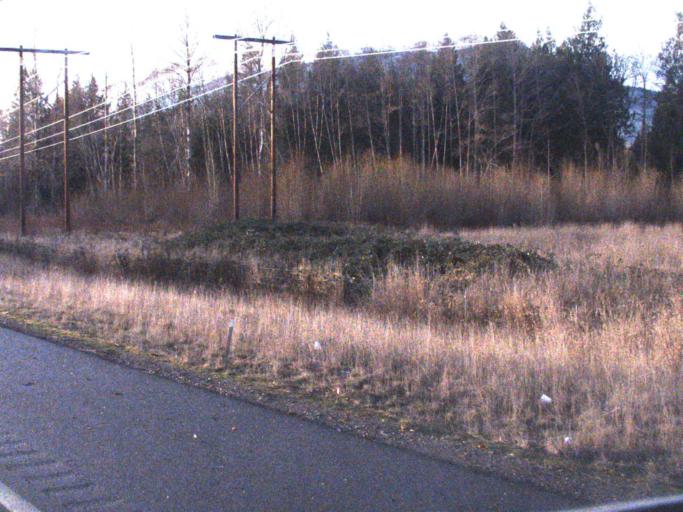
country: US
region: Washington
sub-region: Skagit County
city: Sedro-Woolley
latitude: 48.5302
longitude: -122.0239
